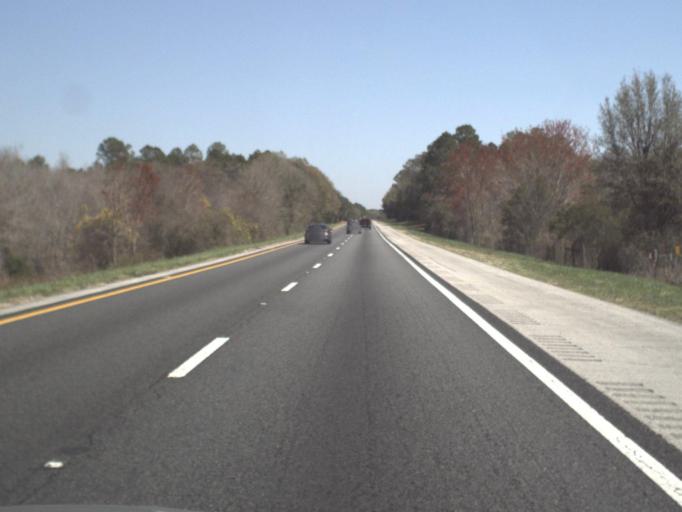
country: US
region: Florida
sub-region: Holmes County
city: Bonifay
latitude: 30.7611
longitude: -85.7222
